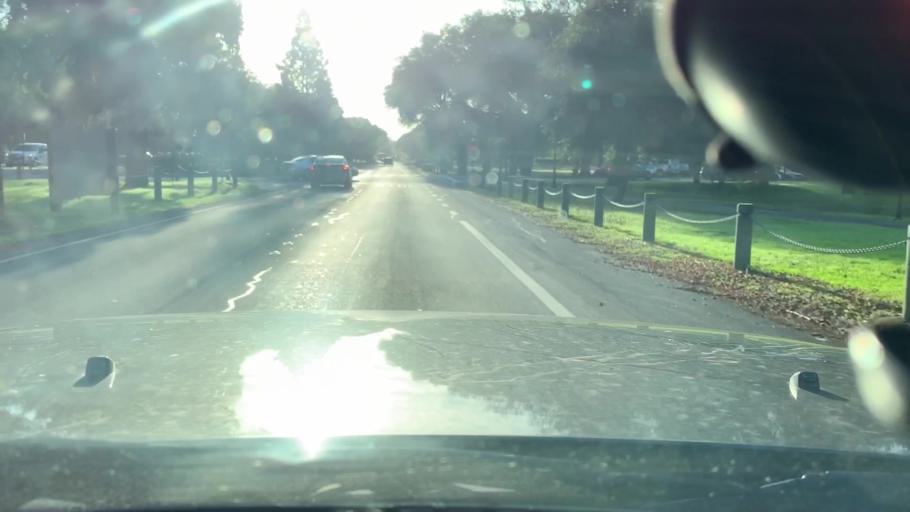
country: US
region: California
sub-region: Santa Clara County
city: Stanford
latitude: 37.4338
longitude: -122.1669
